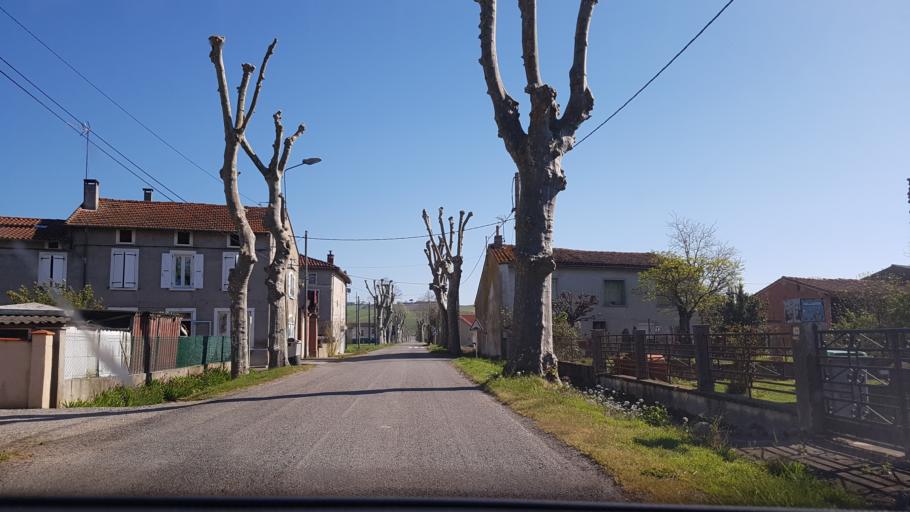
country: FR
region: Midi-Pyrenees
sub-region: Departement de l'Ariege
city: Mazeres
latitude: 43.2553
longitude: 1.6829
